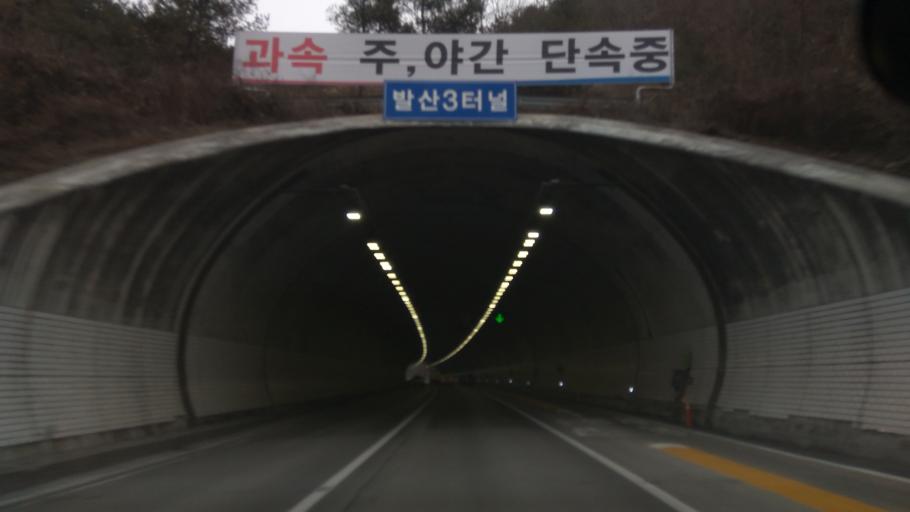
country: KR
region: Gangwon-do
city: Sindong
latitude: 37.7302
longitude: 127.6128
